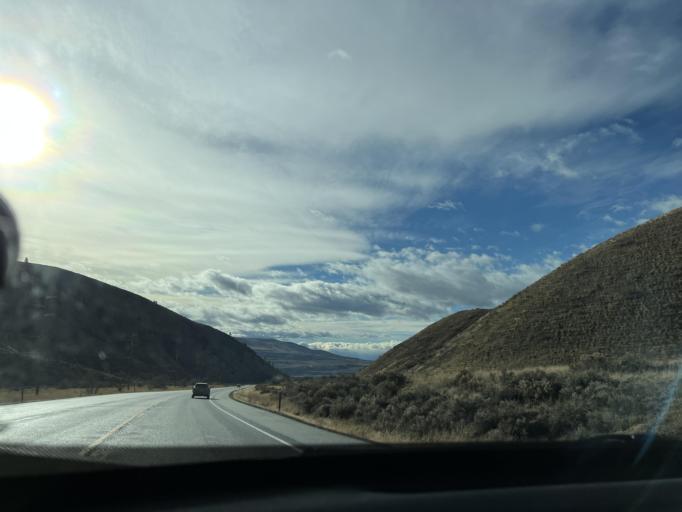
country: US
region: Washington
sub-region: Chelan County
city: Manson
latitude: 47.7994
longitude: -120.1328
